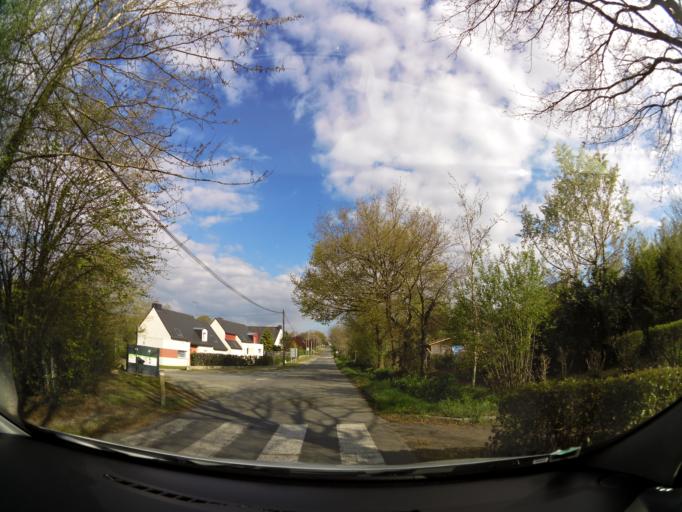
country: FR
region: Brittany
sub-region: Departement d'Ille-et-Vilaine
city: Laille
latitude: 47.9728
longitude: -1.7141
